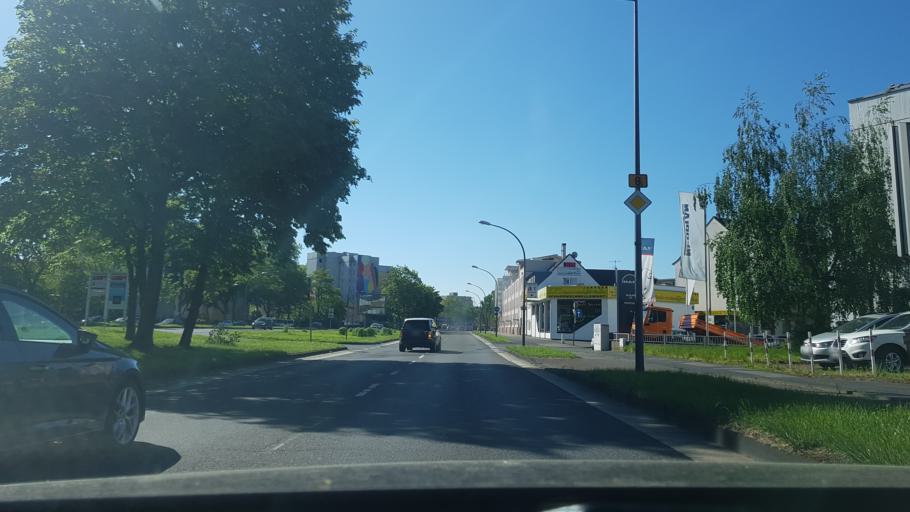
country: DE
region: North Rhine-Westphalia
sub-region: Regierungsbezirk Koln
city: Muelheim
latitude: 50.9755
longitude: 7.0047
